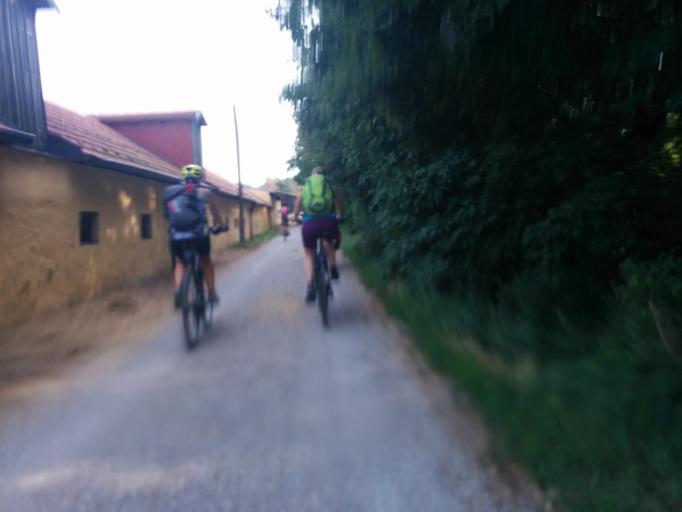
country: AT
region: Lower Austria
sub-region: Politischer Bezirk Modling
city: Gumpoldskirchen
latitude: 48.0557
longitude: 16.2734
